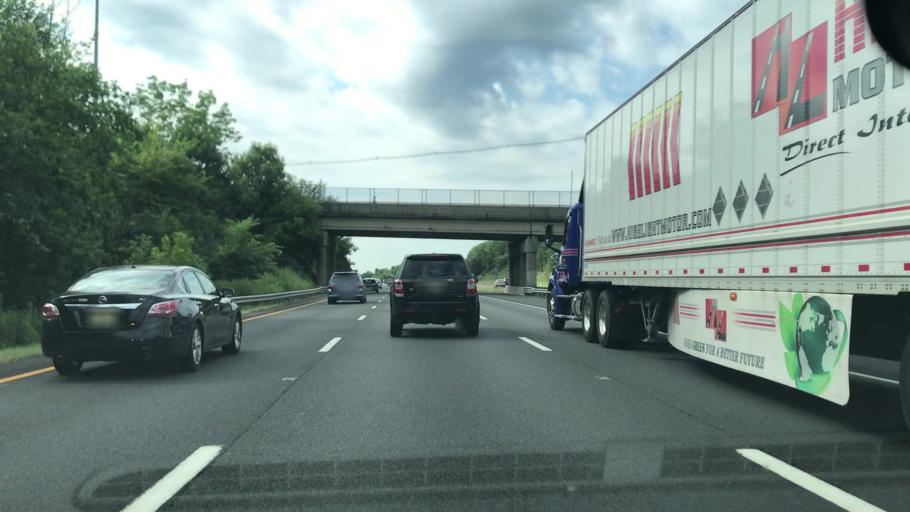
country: US
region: New Jersey
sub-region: Somerset County
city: Bridgewater
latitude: 40.6276
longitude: -74.6420
